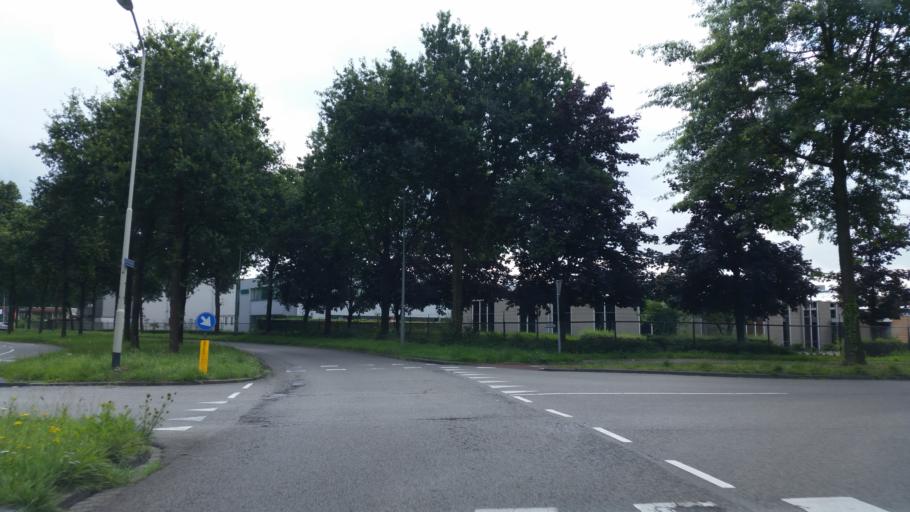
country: NL
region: North Brabant
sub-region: Gemeente Breda
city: Breda
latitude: 51.6115
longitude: 4.7206
